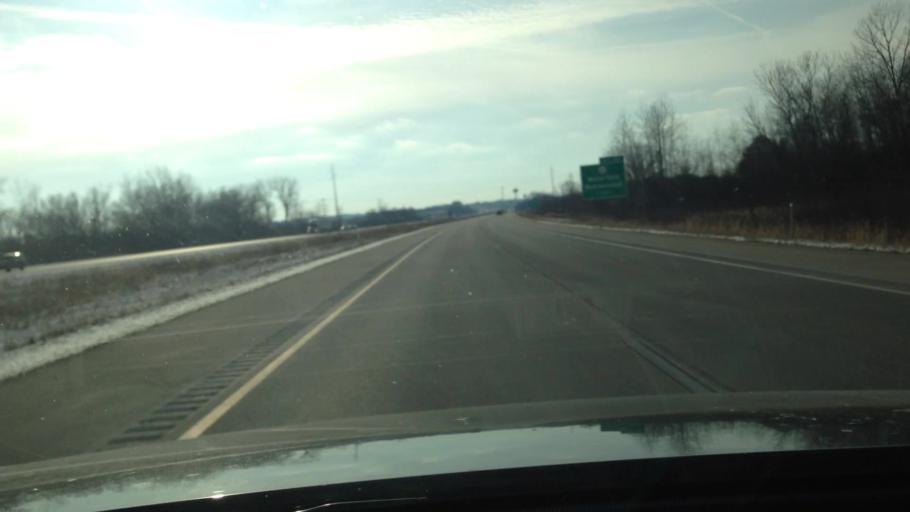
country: US
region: Wisconsin
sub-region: Waukesha County
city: Mukwonago
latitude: 42.8656
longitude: -88.2998
